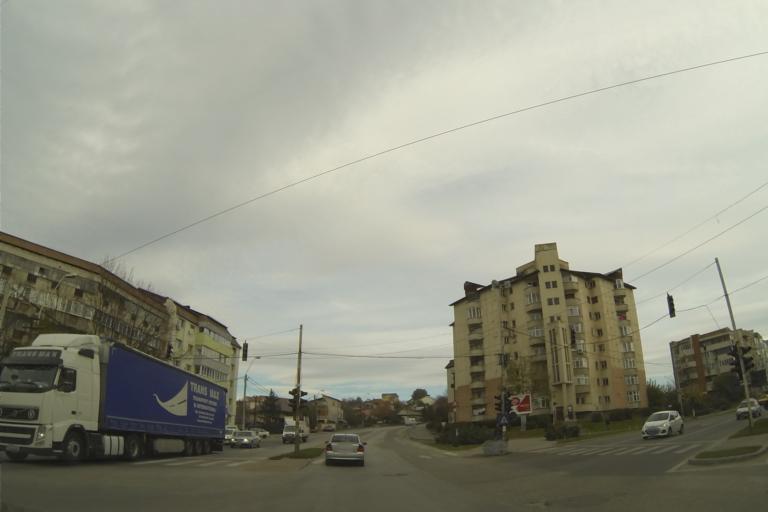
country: RO
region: Olt
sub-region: Municipiul Slatina
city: Slatina
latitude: 44.4313
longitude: 24.3554
